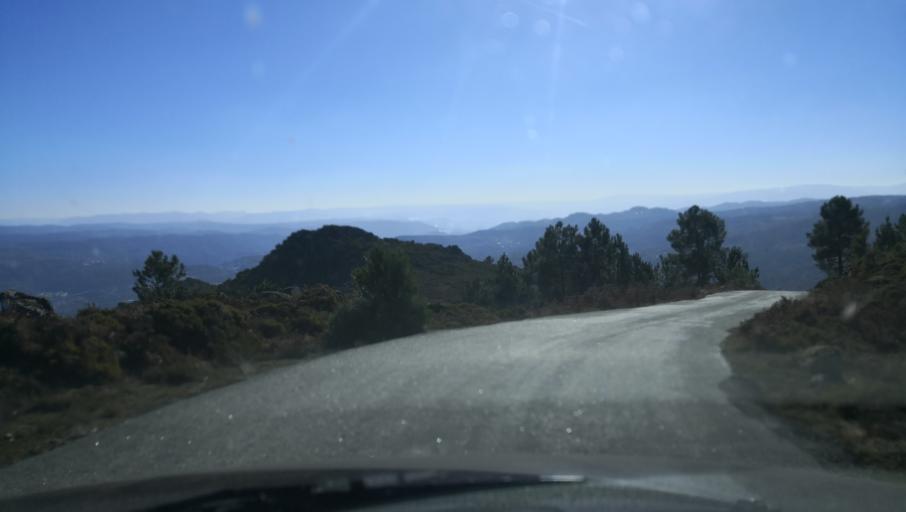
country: PT
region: Vila Real
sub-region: Vila Real
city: Vila Real
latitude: 41.3264
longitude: -7.7897
